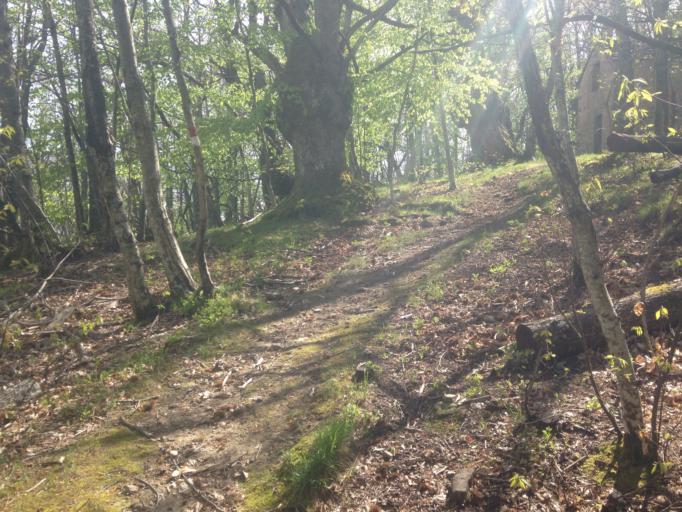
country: IT
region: Emilia-Romagna
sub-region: Provincia di Bologna
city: Lizzano in Belvedere
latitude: 44.1604
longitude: 10.8858
